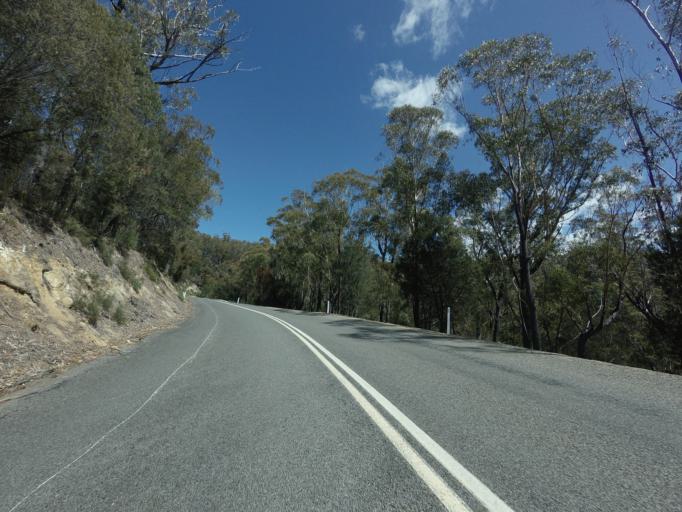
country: AU
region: Tasmania
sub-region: Break O'Day
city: St Helens
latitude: -41.6647
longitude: 148.2641
